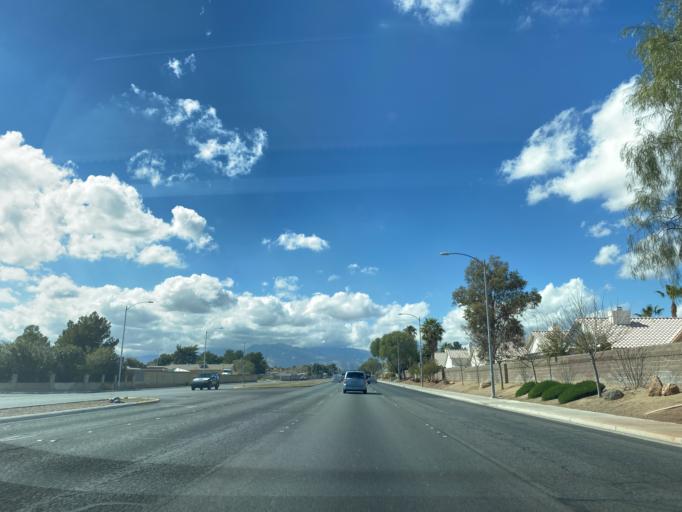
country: US
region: Nevada
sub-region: Clark County
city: Las Vegas
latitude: 36.2389
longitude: -115.2115
